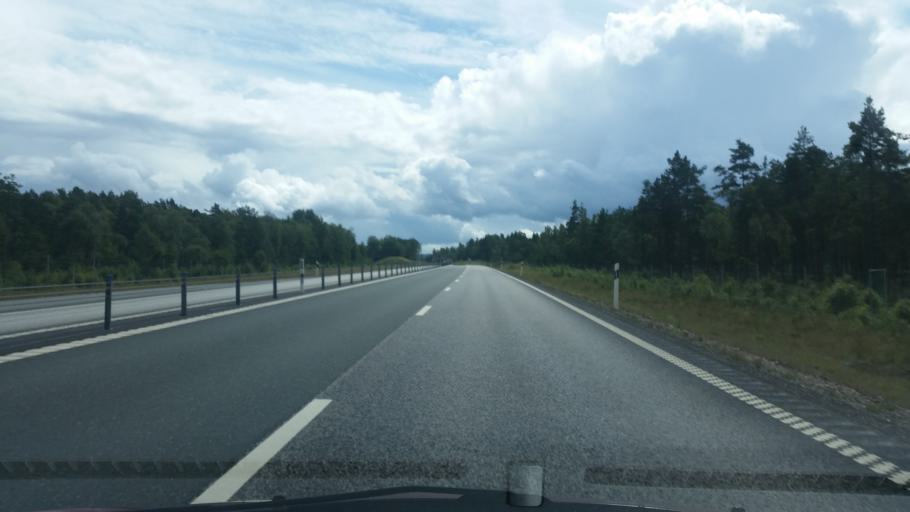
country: SE
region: Joenkoeping
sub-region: Gislaveds Kommun
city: Gislaved
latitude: 57.2962
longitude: 13.5880
